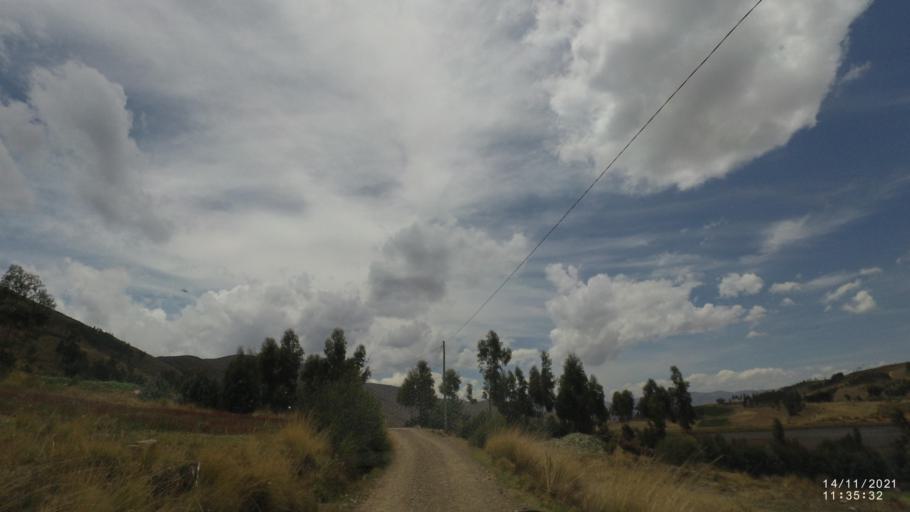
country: BO
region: Cochabamba
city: Colomi
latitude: -17.3458
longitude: -66.0010
